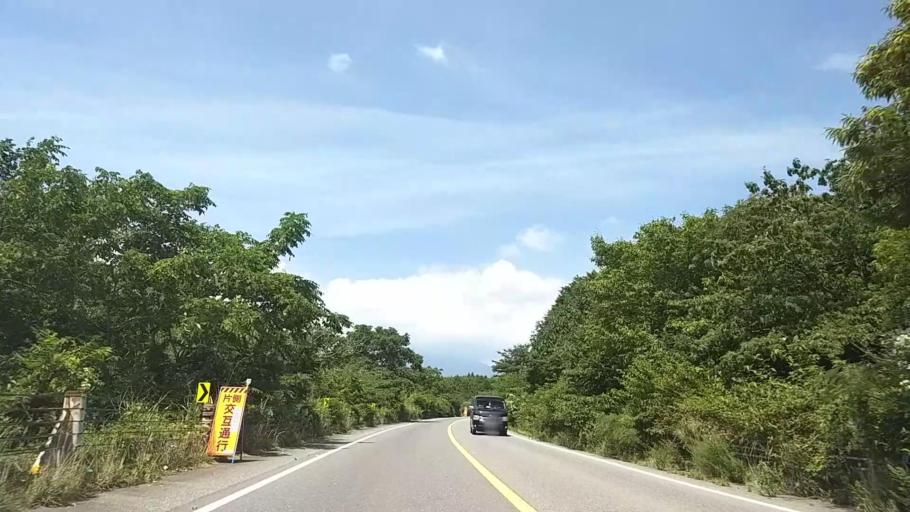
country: JP
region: Shizuoka
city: Fujinomiya
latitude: 35.3197
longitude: 138.5908
